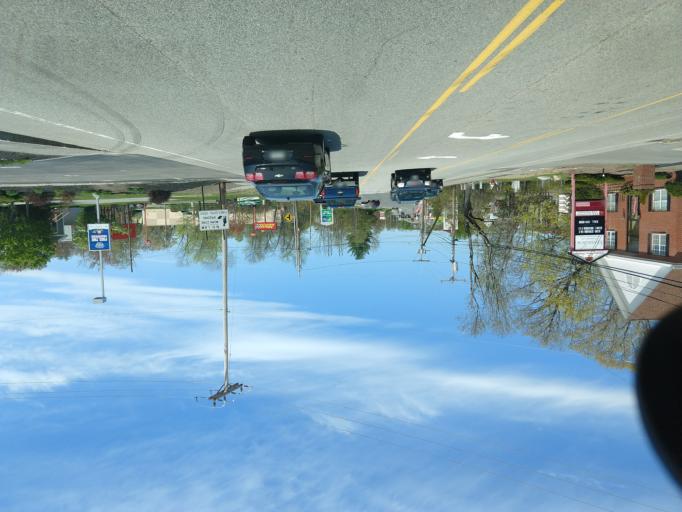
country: US
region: New Hampshire
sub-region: Rockingham County
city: Seabrook
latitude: 42.8961
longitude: -70.8706
